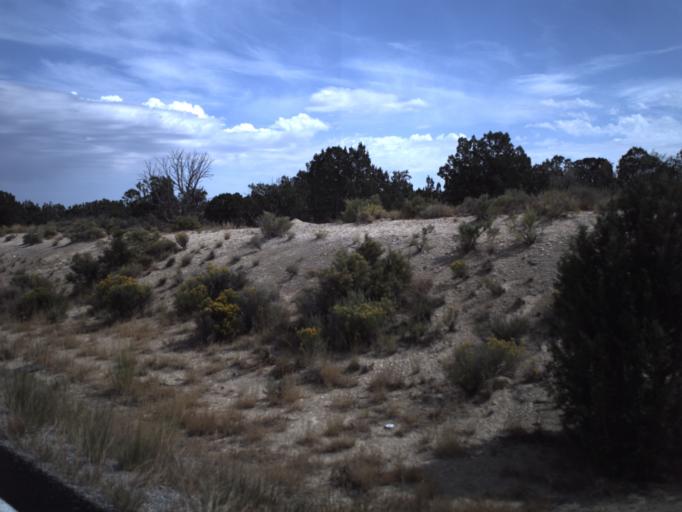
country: US
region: Idaho
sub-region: Cassia County
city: Burley
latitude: 41.7856
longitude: -113.4795
